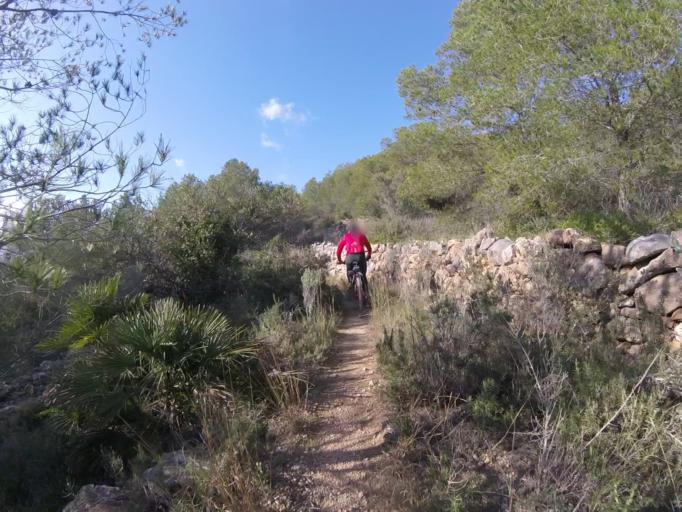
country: ES
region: Valencia
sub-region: Provincia de Castello
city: Santa Magdalena de Pulpis
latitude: 40.2982
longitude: 0.3279
